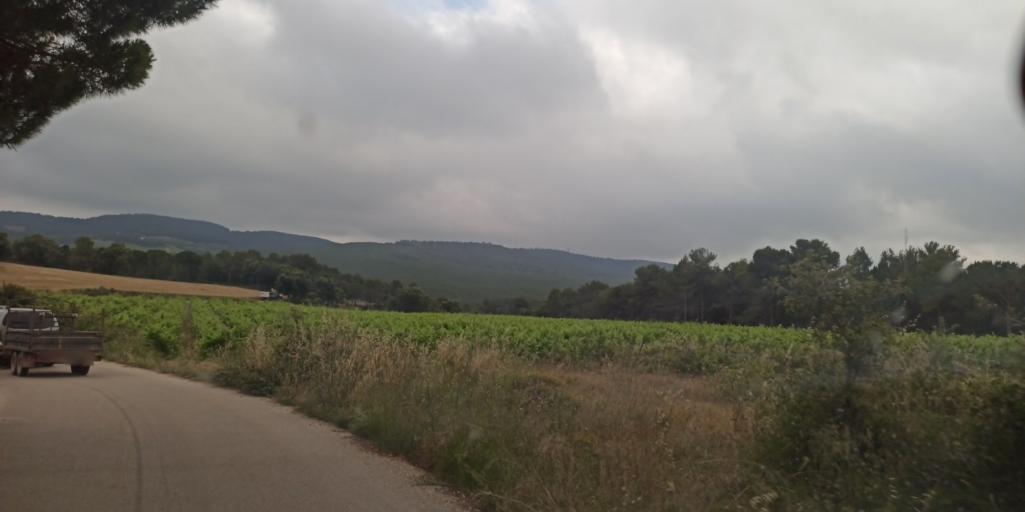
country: ES
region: Catalonia
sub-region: Provincia de Tarragona
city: Querol
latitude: 41.4247
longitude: 1.4998
